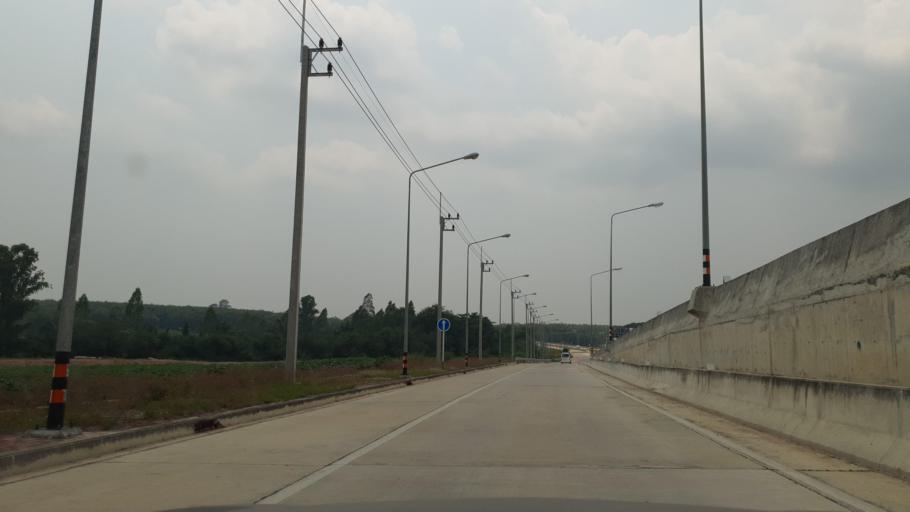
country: TH
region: Chon Buri
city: Phatthaya
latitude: 12.8394
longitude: 100.9598
